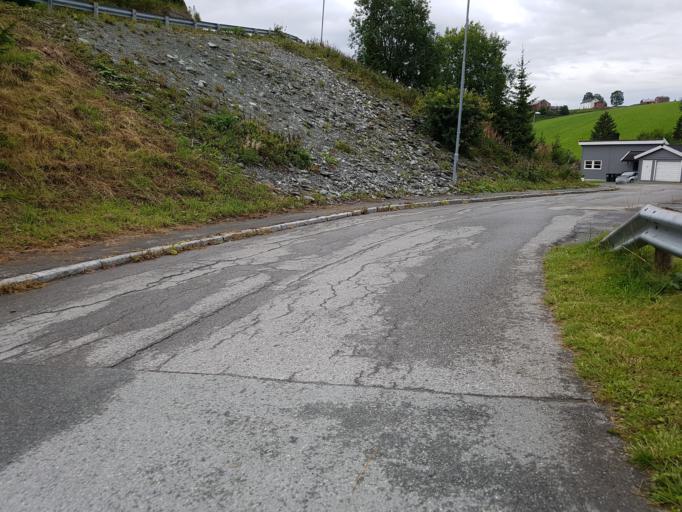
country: NO
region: Sor-Trondelag
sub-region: Trondheim
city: Trondheim
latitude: 63.3845
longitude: 10.3415
